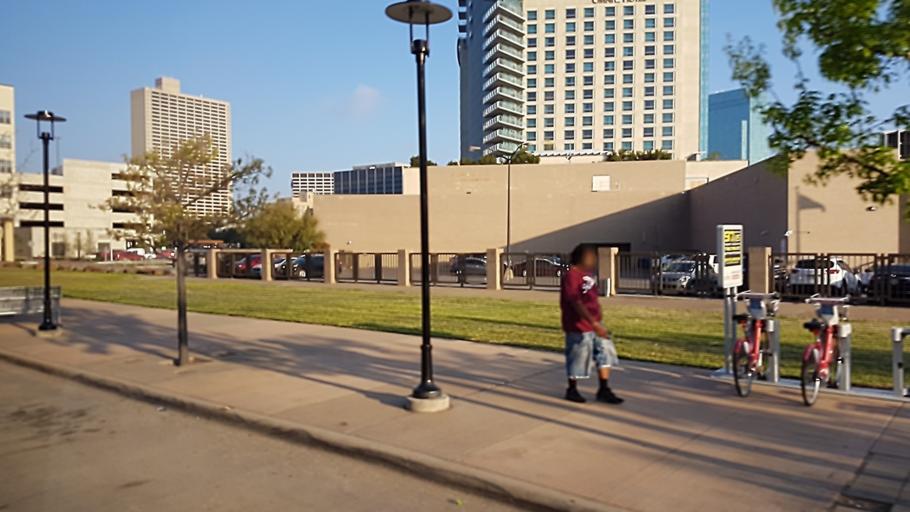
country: US
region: Texas
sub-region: Tarrant County
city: Fort Worth
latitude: 32.7467
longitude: -97.3274
